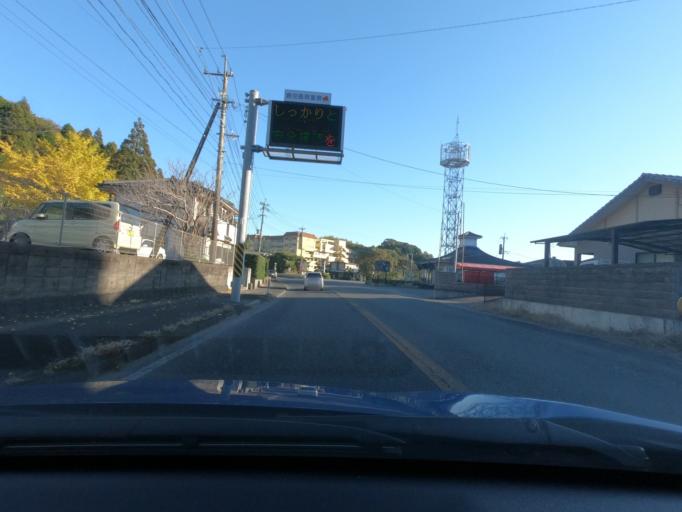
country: JP
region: Kagoshima
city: Satsumasendai
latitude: 31.8611
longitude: 130.2278
